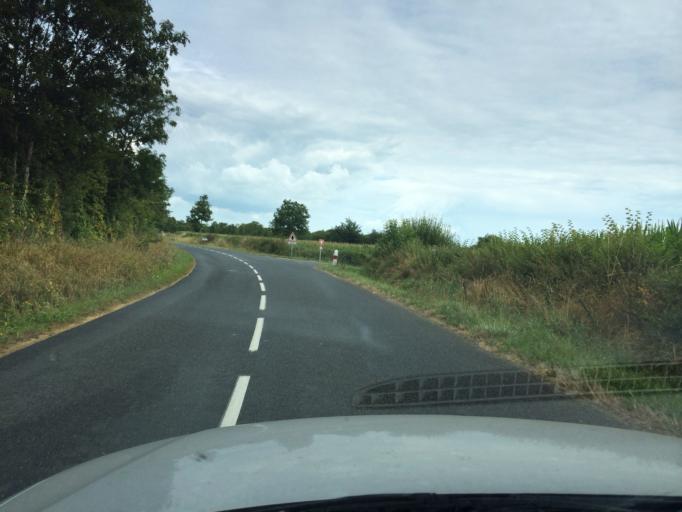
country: FR
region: Lower Normandy
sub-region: Departement de la Manche
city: Sainte-Mere-Eglise
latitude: 49.4408
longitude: -1.2871
